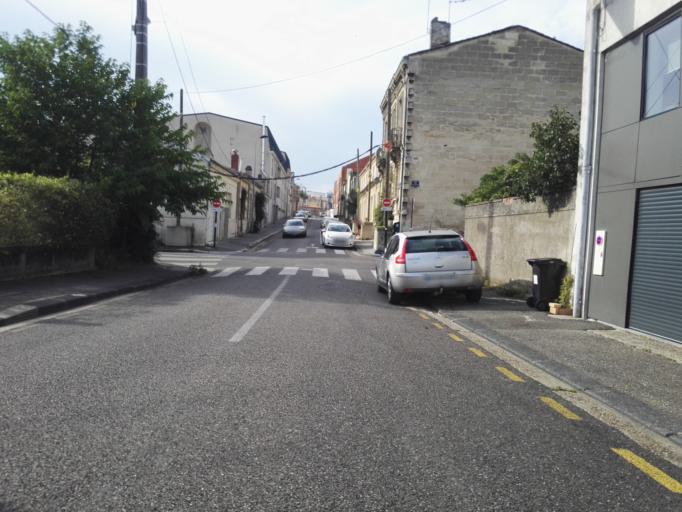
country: FR
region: Aquitaine
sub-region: Departement de la Gironde
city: Begles
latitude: 44.8118
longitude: -0.5698
